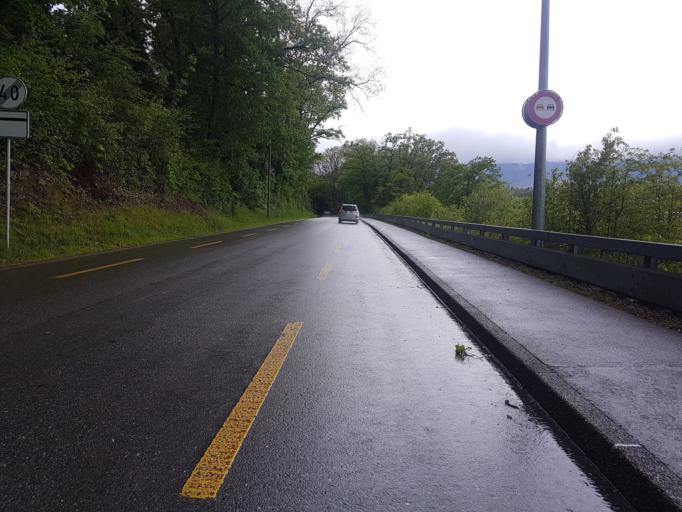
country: CH
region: Geneva
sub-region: Geneva
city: Dardagny
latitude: 46.1753
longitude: 5.9998
